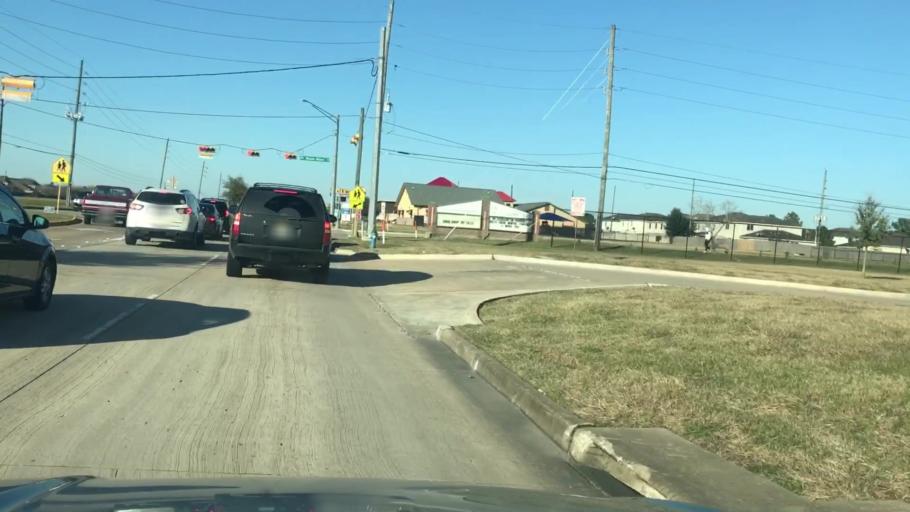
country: US
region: Texas
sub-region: Fort Bend County
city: Cinco Ranch
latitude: 29.8090
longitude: -95.7520
